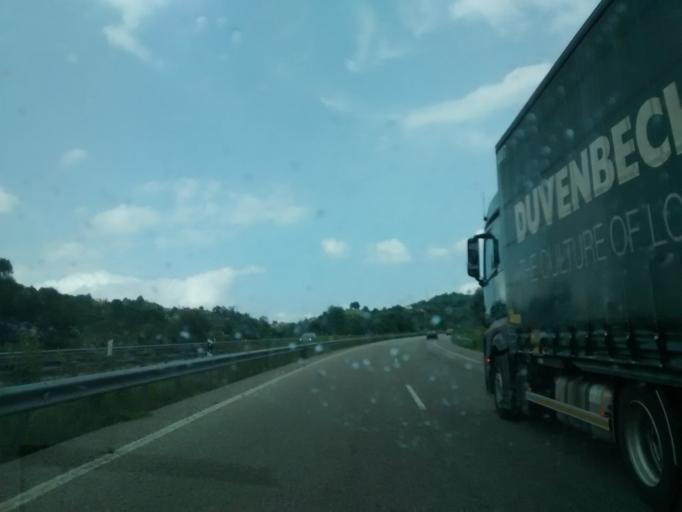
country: ES
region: Asturias
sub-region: Province of Asturias
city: Mieres
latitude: 43.2792
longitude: -5.7657
